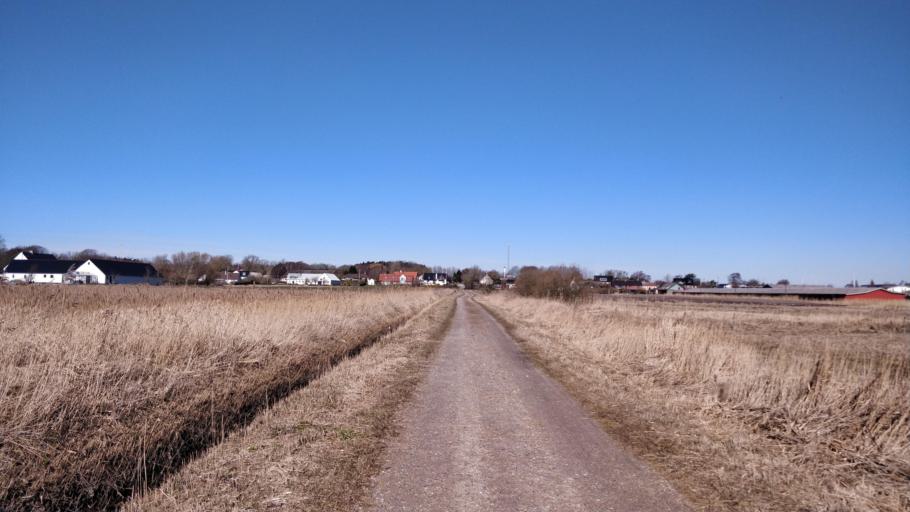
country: DK
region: North Denmark
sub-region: Jammerbugt Kommune
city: Abybro
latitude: 57.0644
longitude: 9.7277
